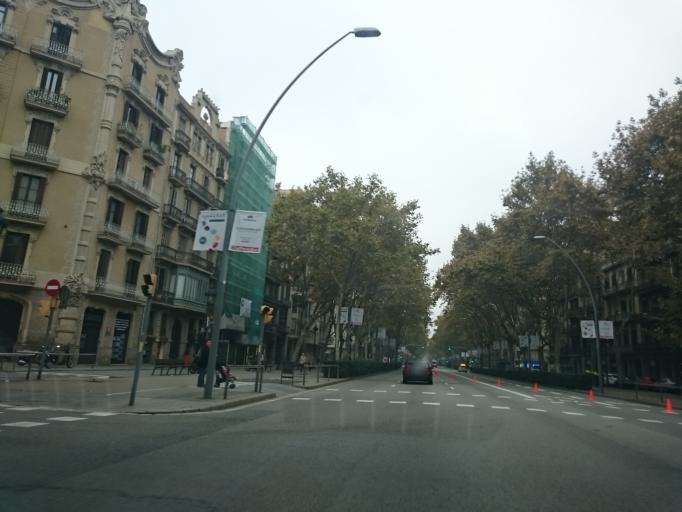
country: ES
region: Catalonia
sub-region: Provincia de Barcelona
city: Sants-Montjuic
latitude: 41.3787
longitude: 2.1539
